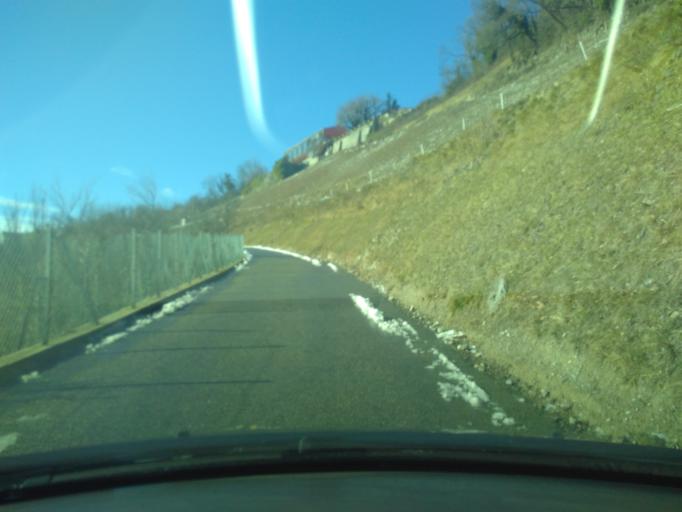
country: FR
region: Rhone-Alpes
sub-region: Departement de l'Isere
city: La Tronche
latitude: 45.2026
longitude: 5.7277
